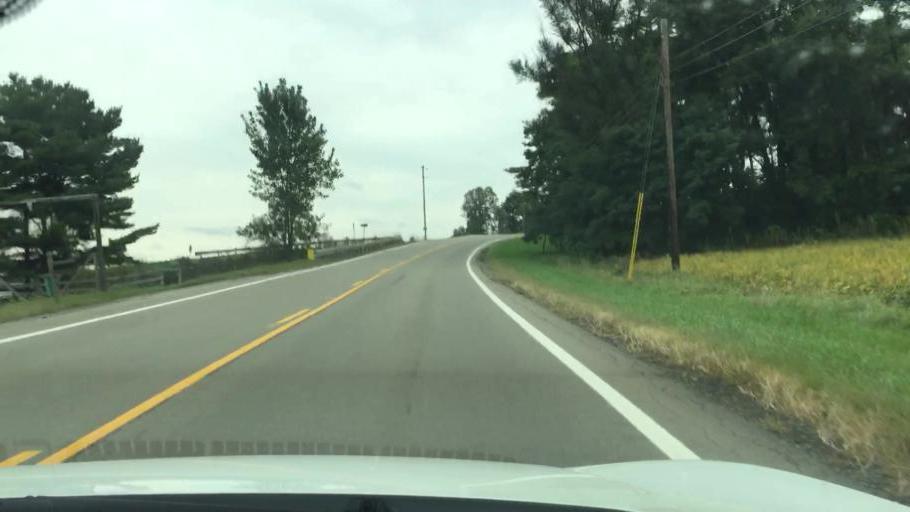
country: US
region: Ohio
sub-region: Champaign County
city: Mechanicsburg
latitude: 40.0460
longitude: -83.6322
